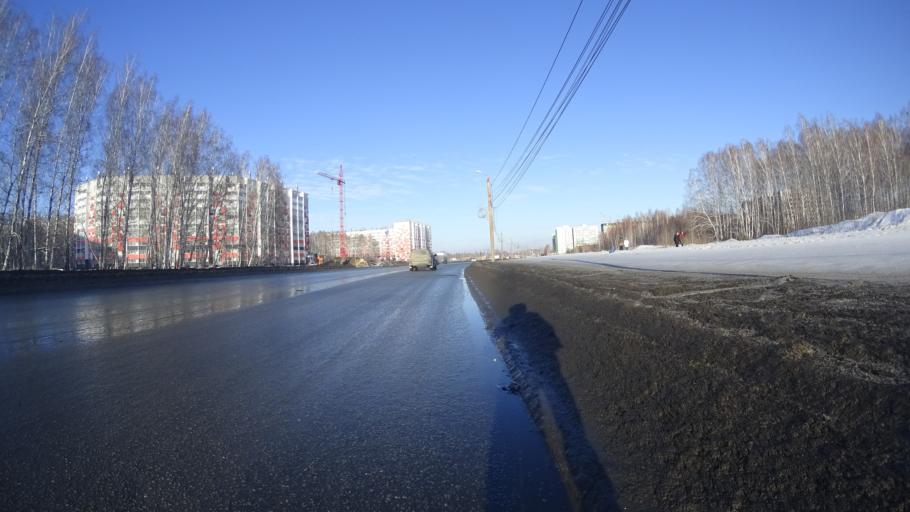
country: RU
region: Chelyabinsk
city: Roshchino
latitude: 55.2156
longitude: 61.2864
